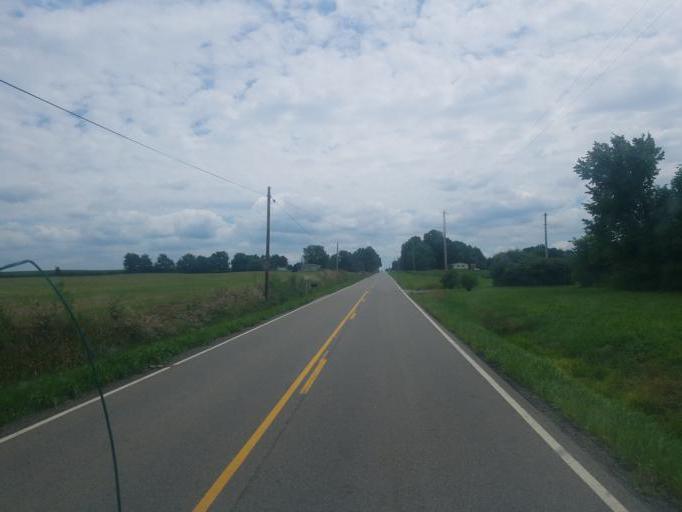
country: US
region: Ohio
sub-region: Licking County
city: Utica
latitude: 40.1850
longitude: -82.5122
